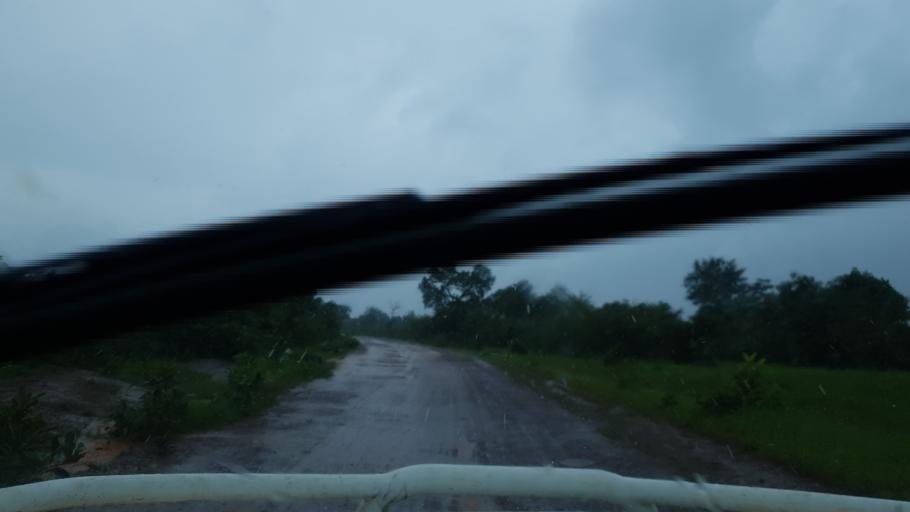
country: ML
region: Sikasso
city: Kolondieba
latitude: 11.6057
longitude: -6.6749
